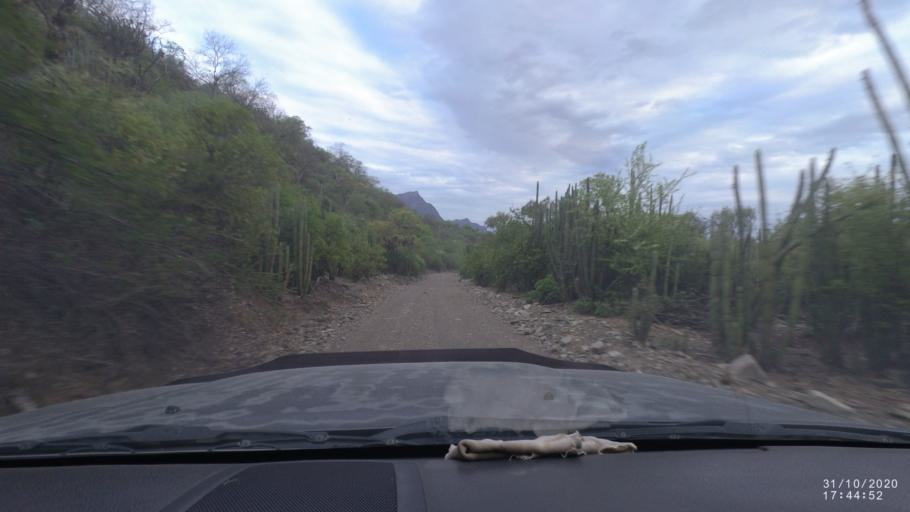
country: BO
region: Chuquisaca
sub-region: Provincia Zudanez
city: Mojocoya
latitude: -18.6124
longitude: -64.5455
